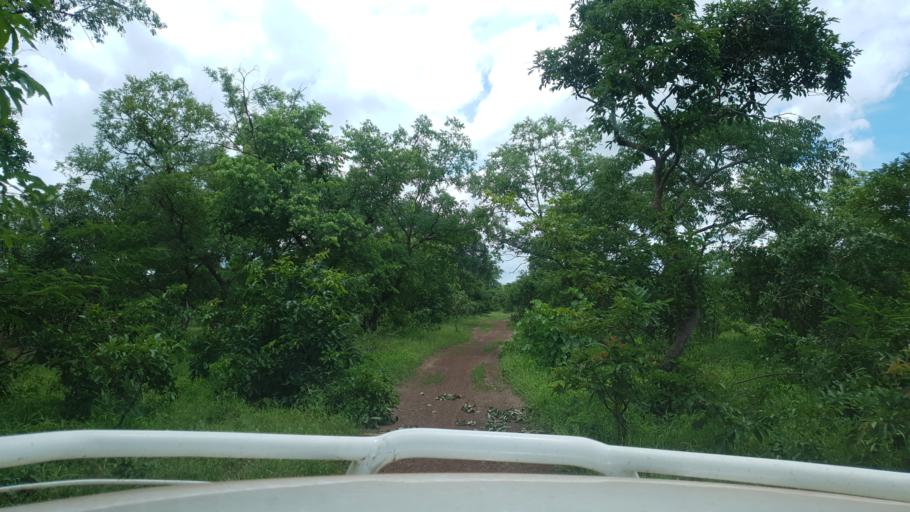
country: ML
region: Koulikoro
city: Banamba
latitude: 13.1963
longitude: -7.3239
